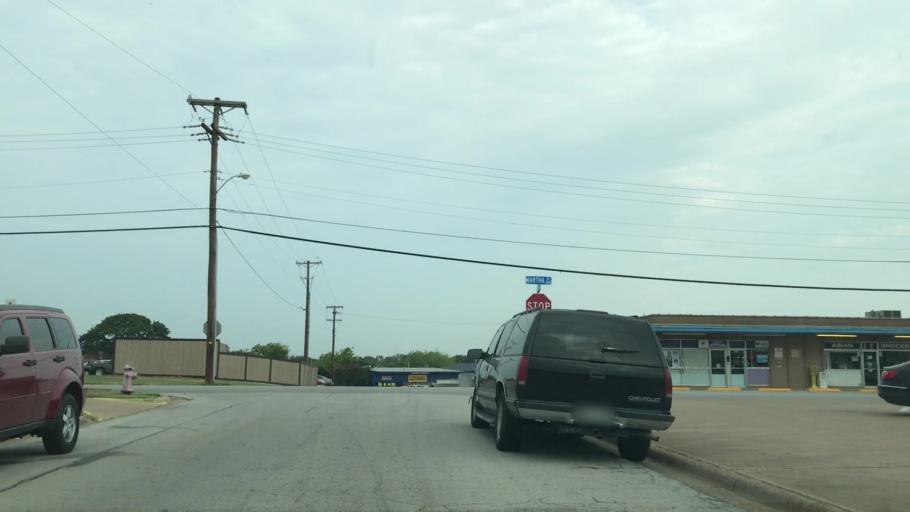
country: US
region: Texas
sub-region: Tarrant County
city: Euless
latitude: 32.8348
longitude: -97.0859
